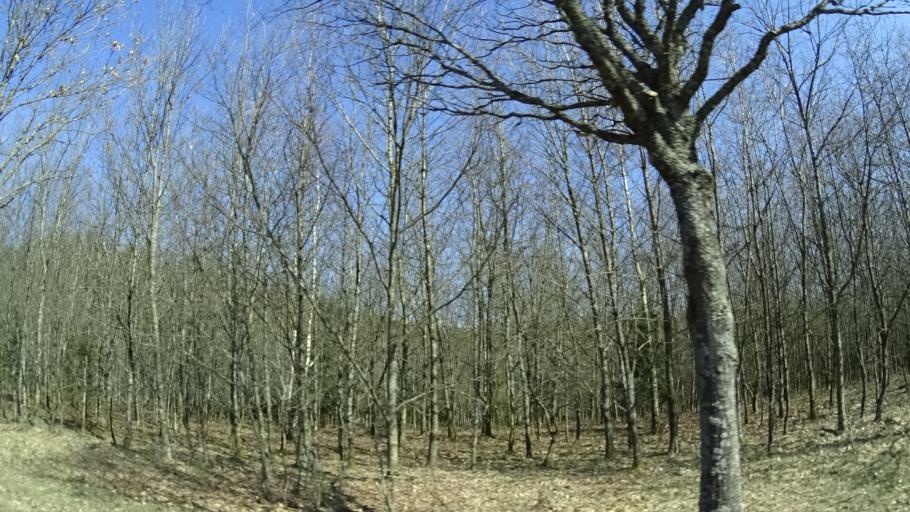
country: DE
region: Rheinland-Pfalz
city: Hattgenstein
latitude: 49.7022
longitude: 7.1520
